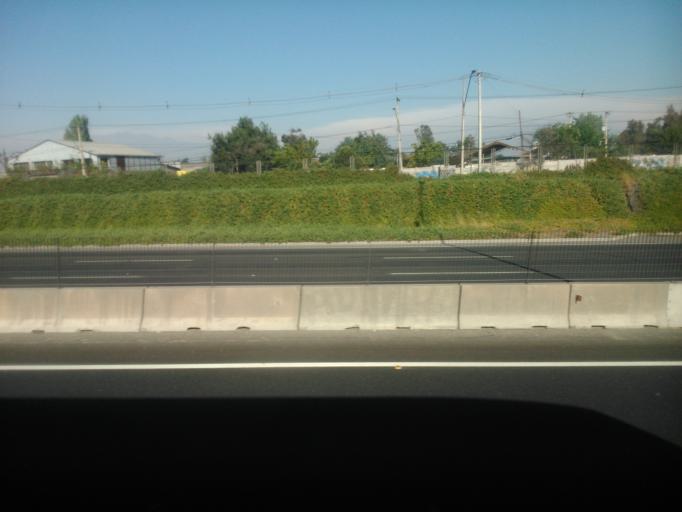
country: CL
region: Santiago Metropolitan
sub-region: Provincia de Maipo
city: San Bernardo
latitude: -33.6063
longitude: -70.7168
